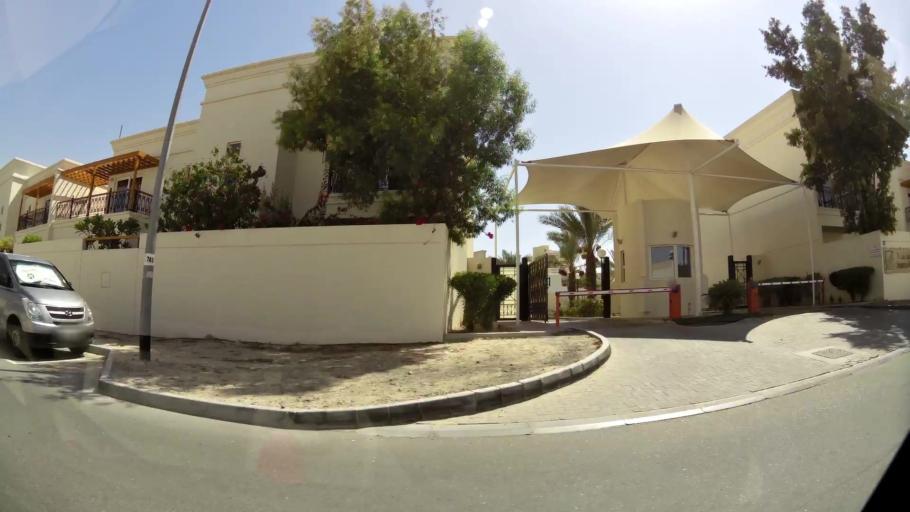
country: AE
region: Dubai
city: Dubai
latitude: 25.1101
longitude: 55.2002
